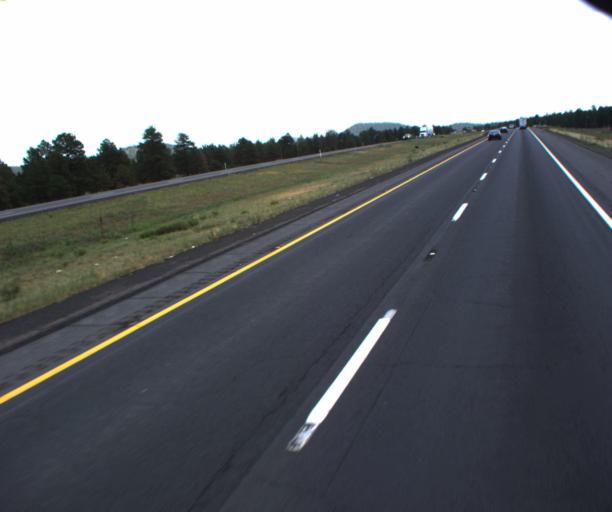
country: US
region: Arizona
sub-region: Coconino County
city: Williams
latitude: 35.2614
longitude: -112.1542
